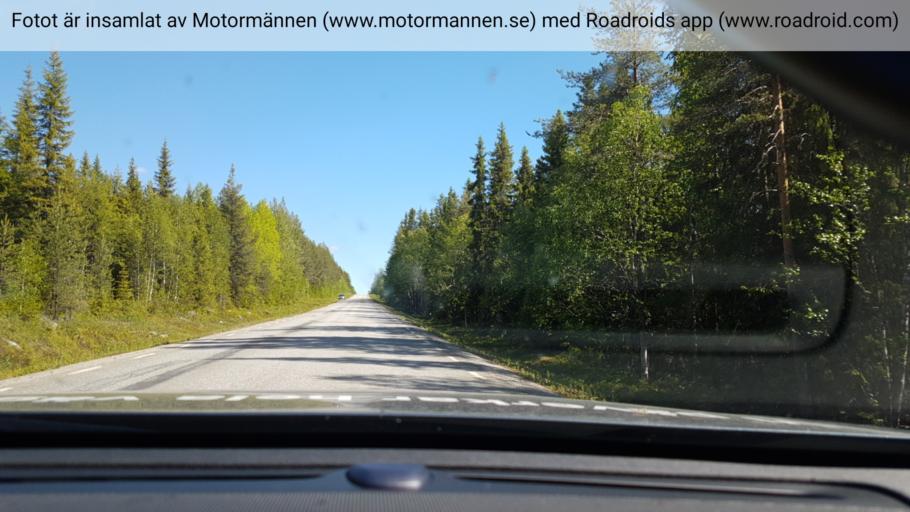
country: SE
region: Vaesterbotten
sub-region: Lycksele Kommun
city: Soderfors
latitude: 64.6881
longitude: 17.7873
